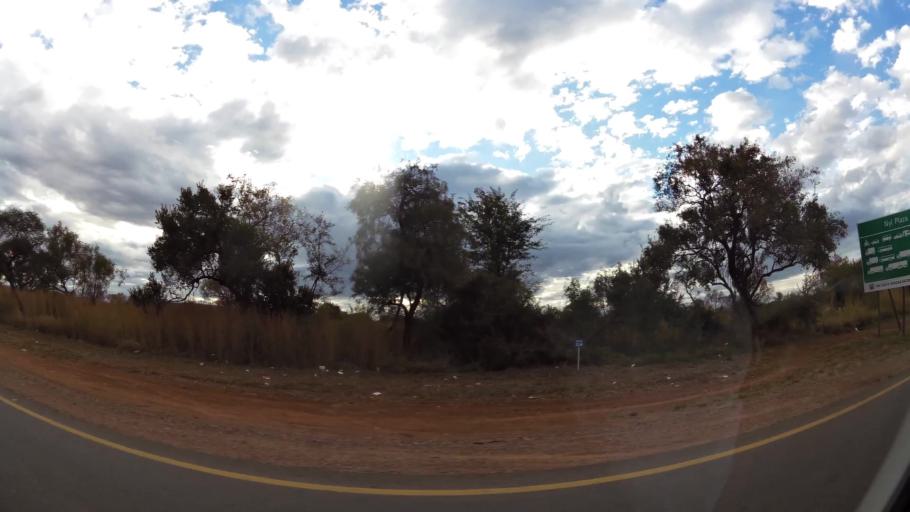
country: ZA
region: Limpopo
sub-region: Waterberg District Municipality
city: Modimolle
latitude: -24.5051
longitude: 28.7289
